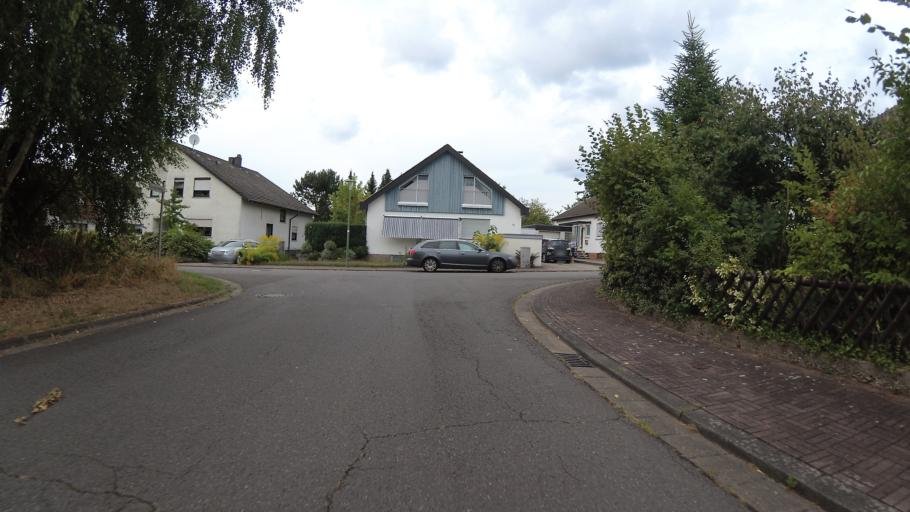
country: DE
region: Saarland
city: Bexbach
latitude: 49.3068
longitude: 7.2763
